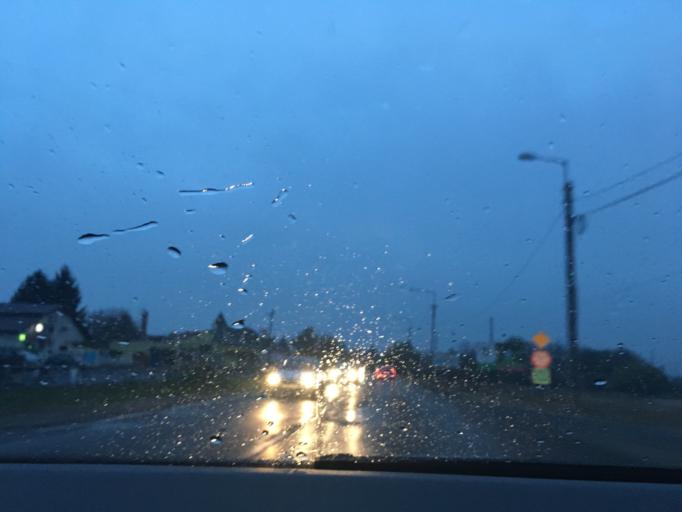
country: HU
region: Pest
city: Nyaregyhaza
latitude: 47.3084
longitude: 19.5004
